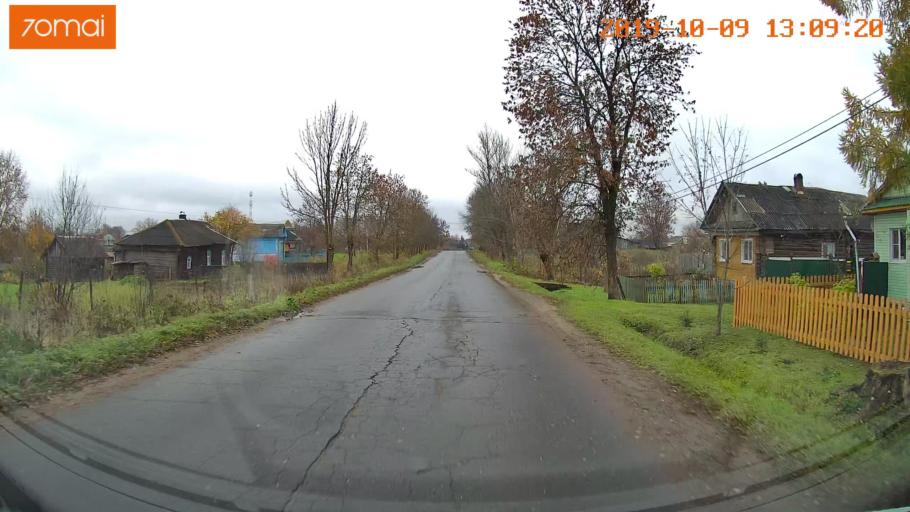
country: RU
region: Jaroslavl
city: Lyubim
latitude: 58.3569
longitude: 40.6746
